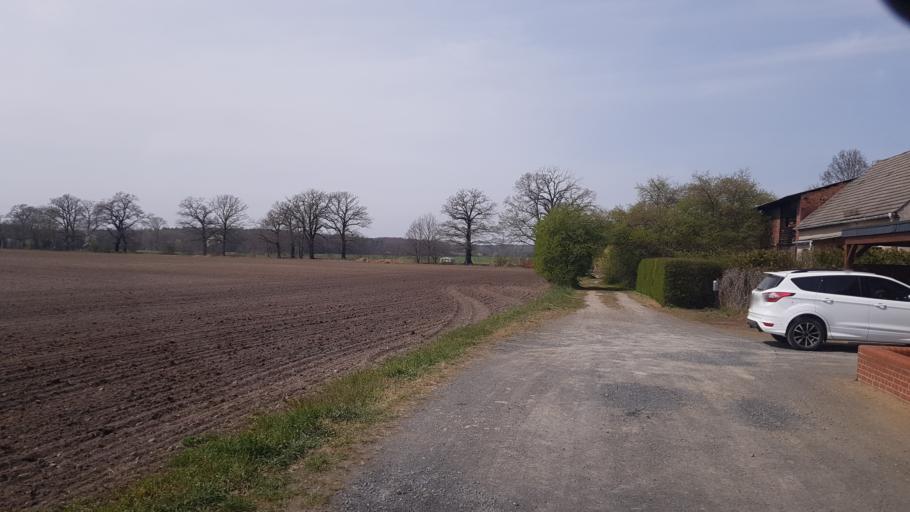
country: DE
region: Brandenburg
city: Doberlug-Kirchhain
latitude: 51.6210
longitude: 13.5580
